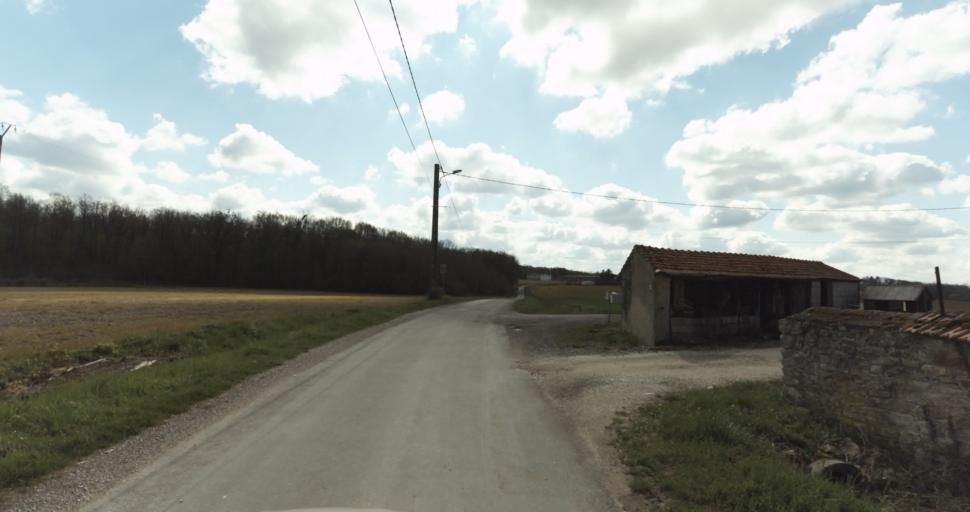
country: FR
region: Bourgogne
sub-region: Departement de la Cote-d'Or
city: Auxonne
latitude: 47.2142
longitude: 5.4298
